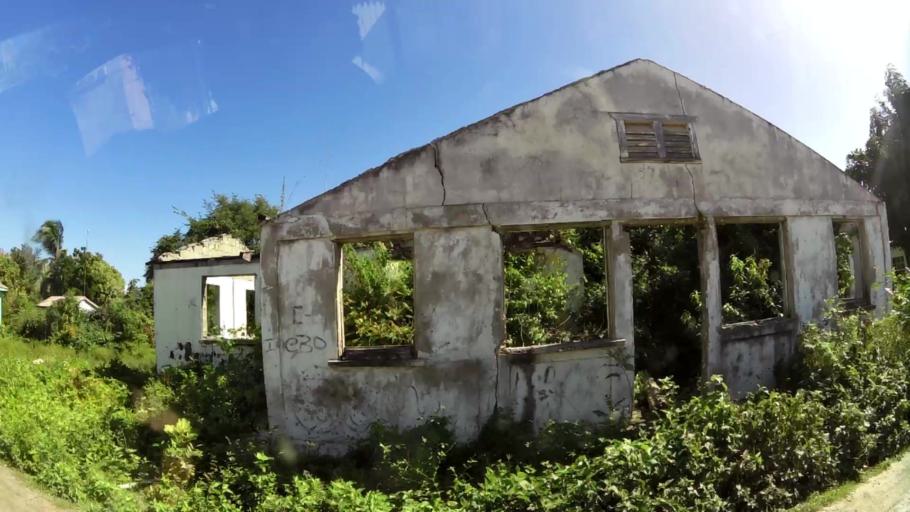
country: AG
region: Barbuda
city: Codrington
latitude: 17.6412
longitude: -61.8241
